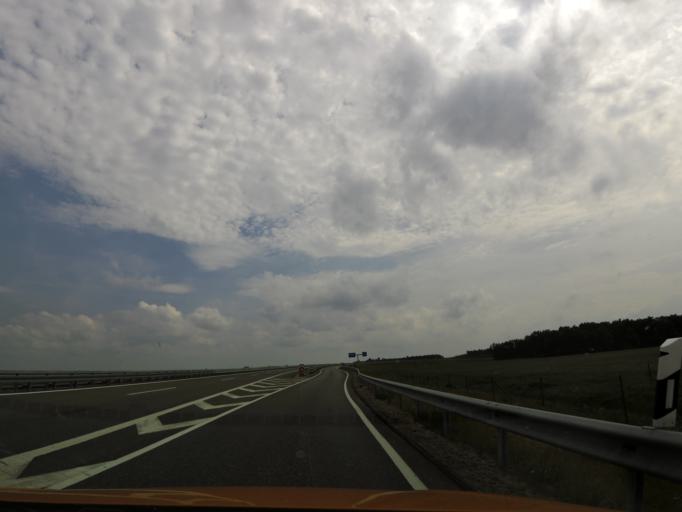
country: DE
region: Mecklenburg-Vorpommern
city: Mirow
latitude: 53.4295
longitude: 11.5169
